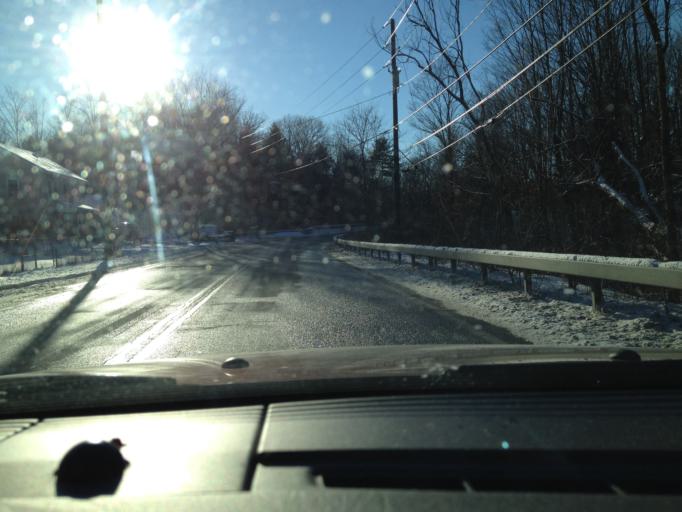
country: US
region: New York
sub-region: Rensselaer County
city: Averill Park
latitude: 42.6279
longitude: -73.5602
